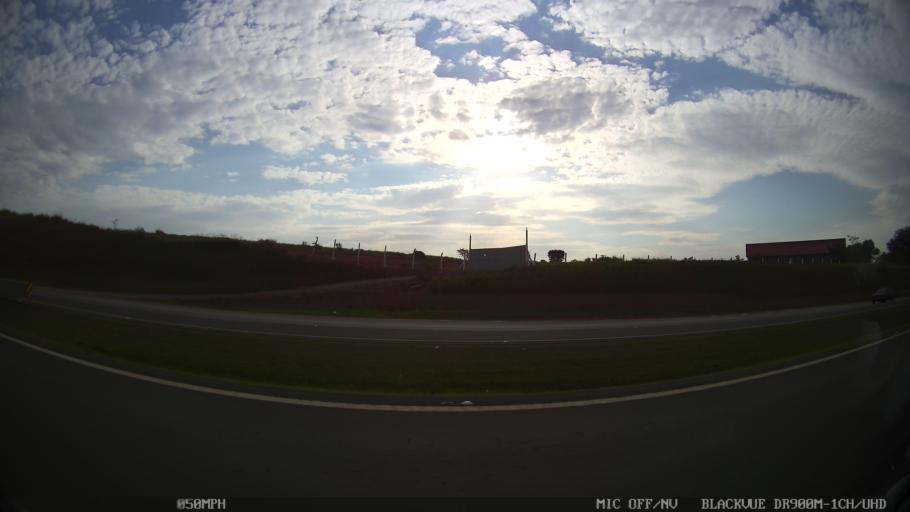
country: BR
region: Sao Paulo
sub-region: Cosmopolis
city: Cosmopolis
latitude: -22.6216
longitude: -47.2001
